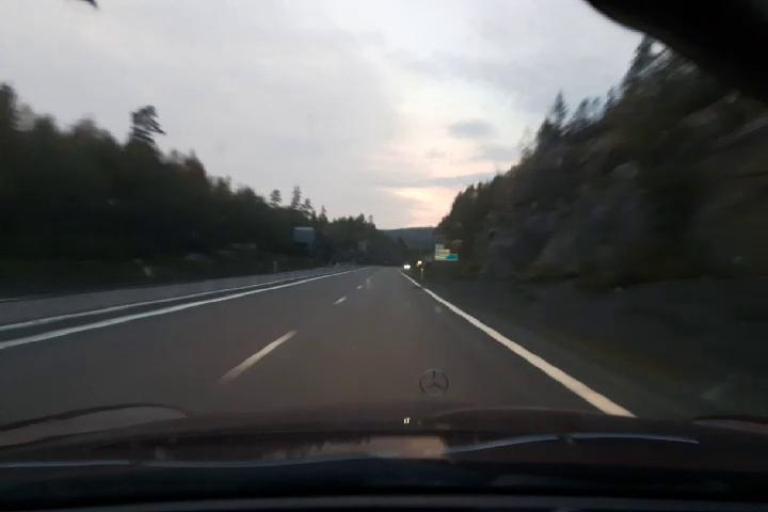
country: SE
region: Vaesternorrland
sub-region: Kramfors Kommun
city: Nordingra
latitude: 62.9477
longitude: 18.0934
